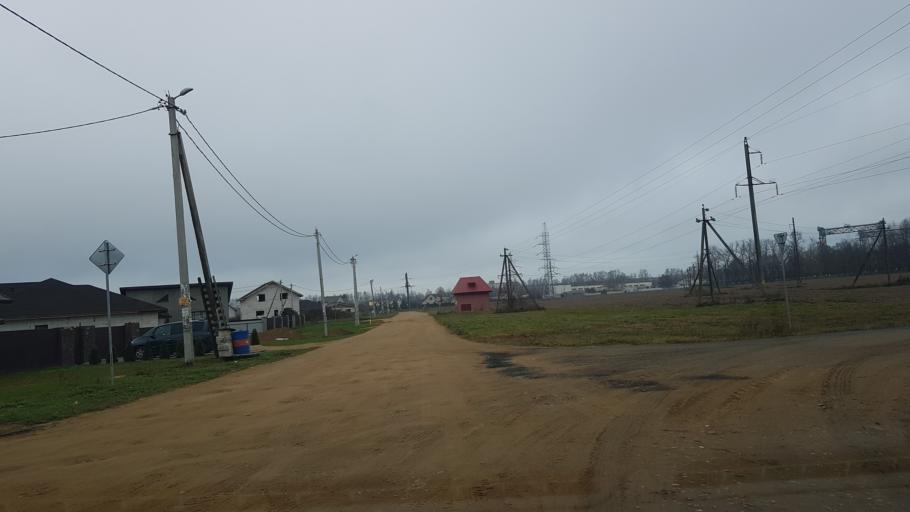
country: BY
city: Fanipol
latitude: 53.7323
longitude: 27.3277
